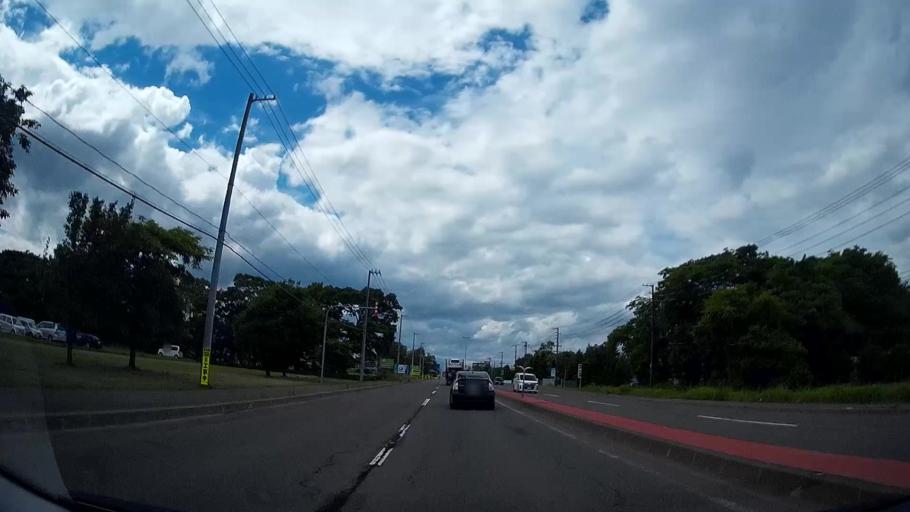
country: JP
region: Hokkaido
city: Chitose
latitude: 42.8672
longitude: 141.5924
